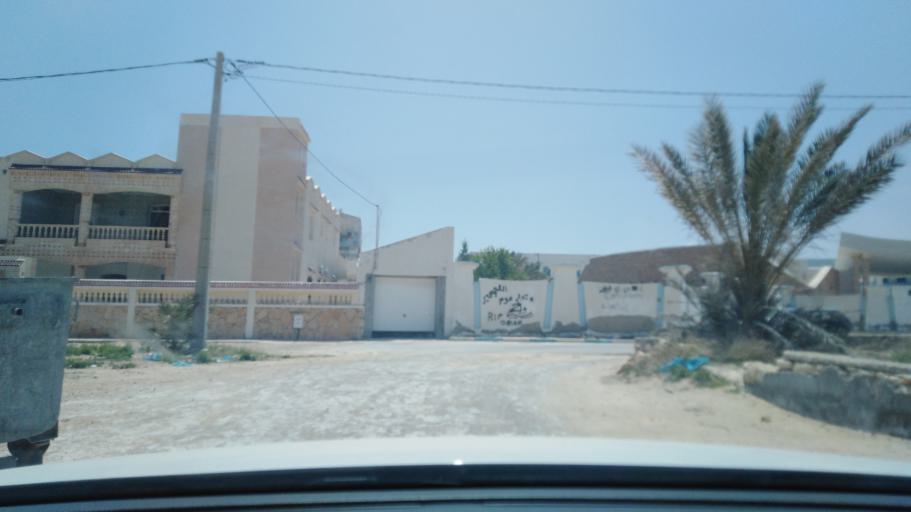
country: TN
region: Qabis
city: Gabes
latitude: 33.9510
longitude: 10.0712
